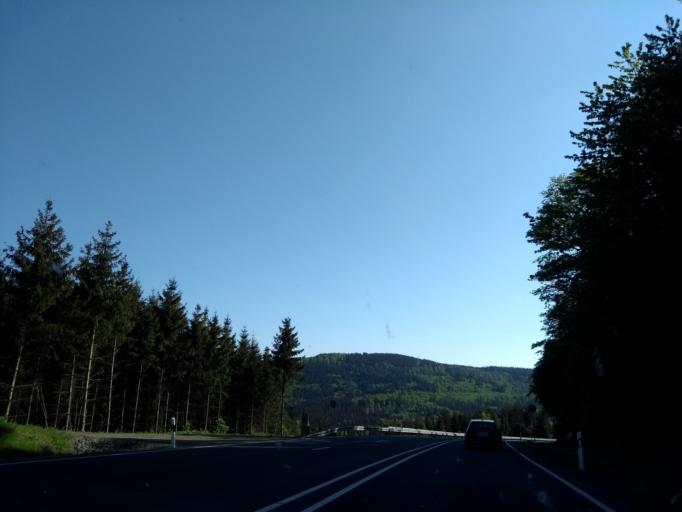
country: DE
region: Hesse
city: Hatzfeld
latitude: 50.9529
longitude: 8.5698
